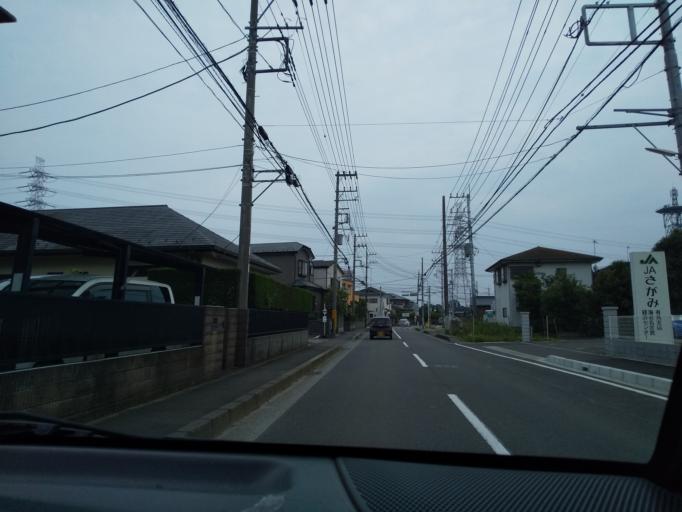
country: JP
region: Kanagawa
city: Atsugi
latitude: 35.4166
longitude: 139.3916
